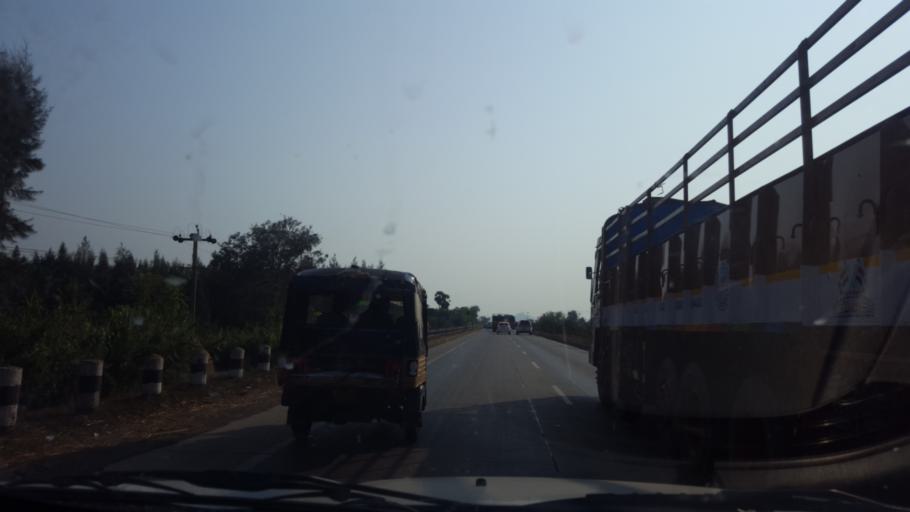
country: IN
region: Andhra Pradesh
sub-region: Vishakhapatnam
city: Elamanchili
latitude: 17.5930
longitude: 82.8712
